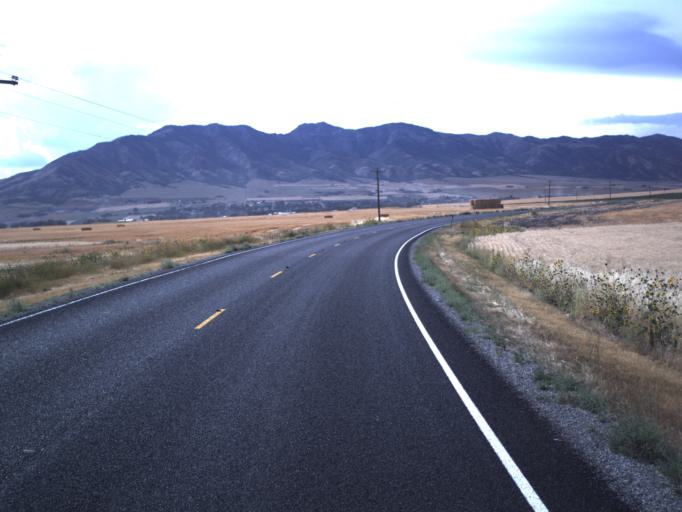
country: US
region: Utah
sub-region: Cache County
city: Benson
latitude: 41.9174
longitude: -112.0005
